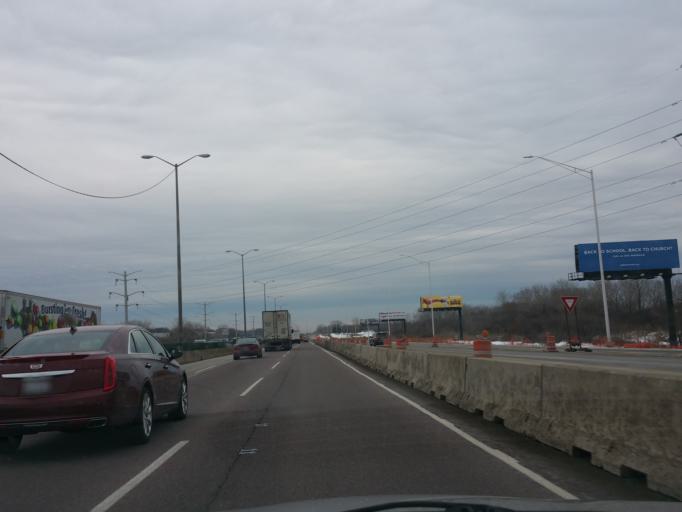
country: US
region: Illinois
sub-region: Cook County
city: South Barrington
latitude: 42.0666
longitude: -88.1362
